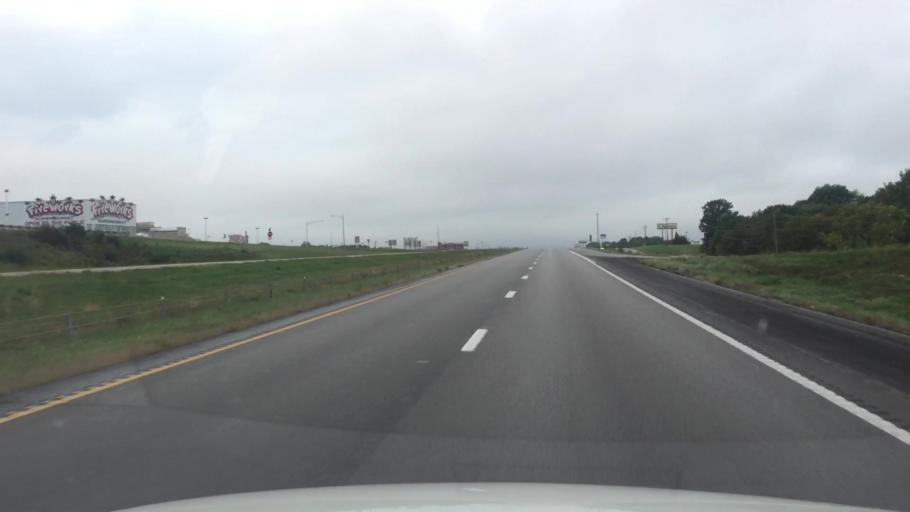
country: US
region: Missouri
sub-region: Lafayette County
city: Odessa
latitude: 39.0087
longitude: -93.9668
